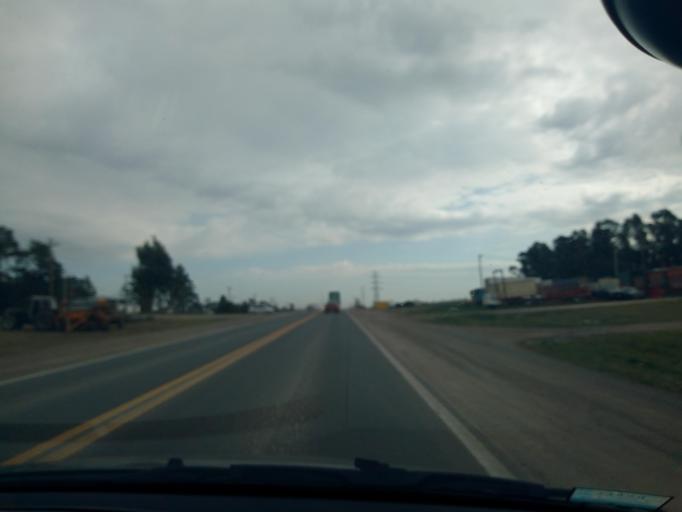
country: AR
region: Buenos Aires
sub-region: Partido de Tandil
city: Tandil
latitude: -37.3232
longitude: -59.0995
